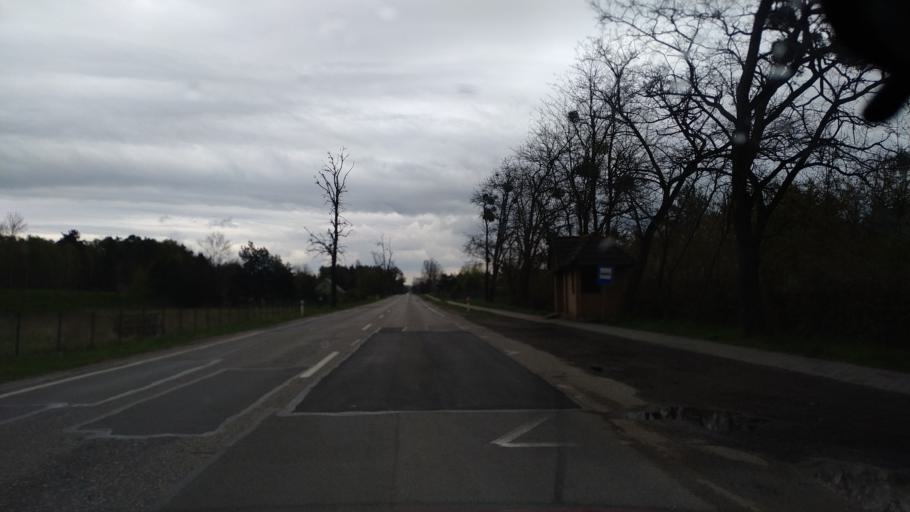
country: PL
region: Pomeranian Voivodeship
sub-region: Powiat tczewski
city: Pelplin
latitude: 54.0262
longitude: 18.6423
